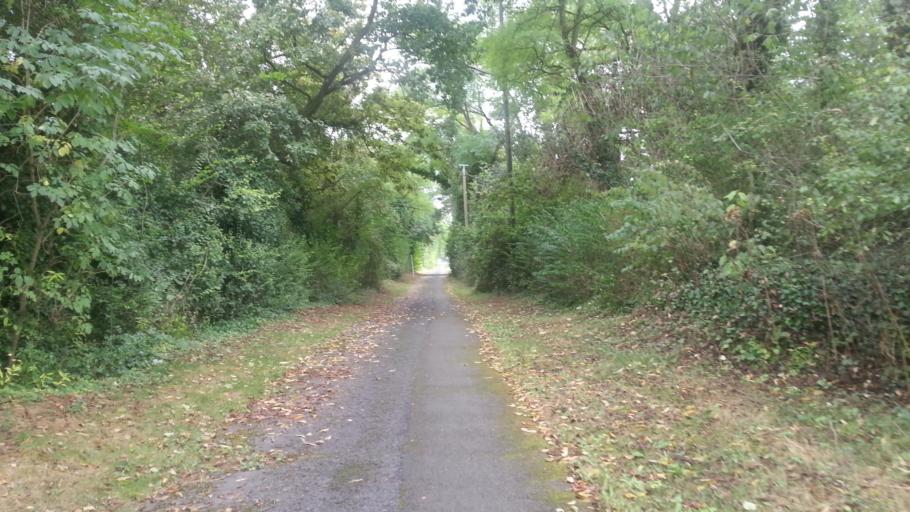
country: FR
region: Picardie
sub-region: Departement de l'Oise
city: Saint-Maximin
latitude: 49.2192
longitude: 2.4491
